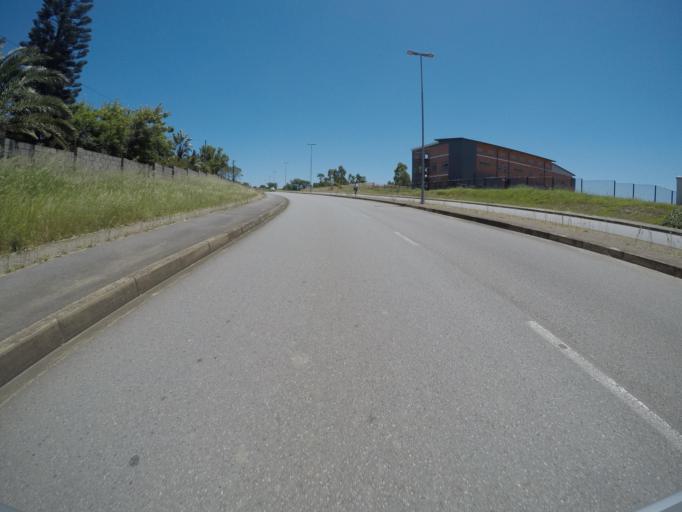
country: ZA
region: Eastern Cape
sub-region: Buffalo City Metropolitan Municipality
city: East London
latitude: -32.9493
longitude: 27.9419
